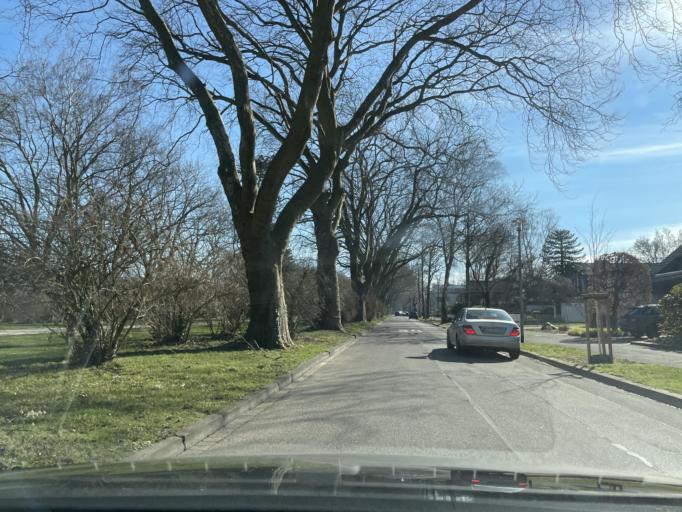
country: DE
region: North Rhine-Westphalia
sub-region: Regierungsbezirk Dusseldorf
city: Monchengladbach
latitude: 51.2088
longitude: 6.4286
